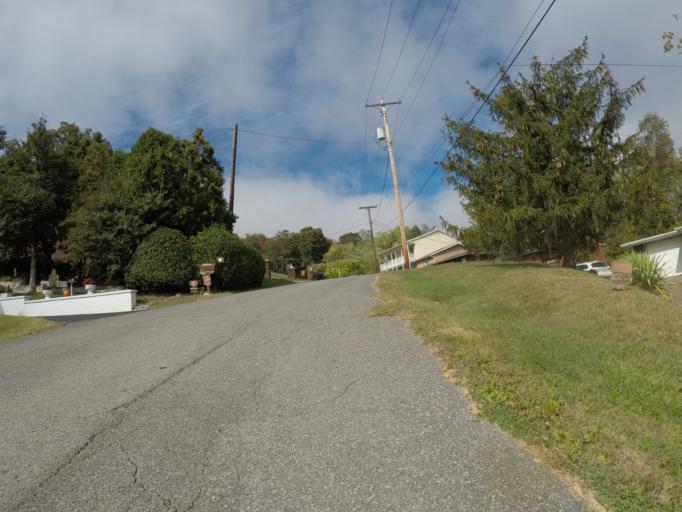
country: US
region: West Virginia
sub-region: Cabell County
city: Huntington
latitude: 38.3969
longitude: -82.3897
